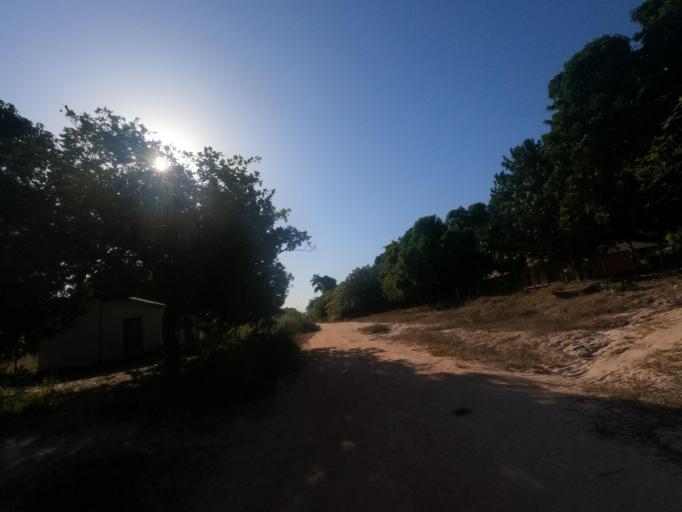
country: GW
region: Cacheu
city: Cacheu
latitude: 12.3934
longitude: -16.2399
